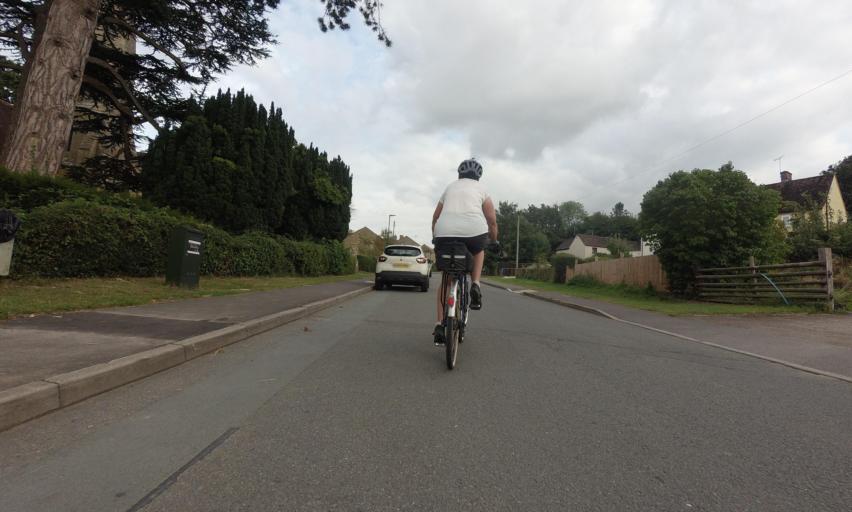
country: GB
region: England
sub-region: Gloucestershire
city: Winchcombe
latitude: 51.9732
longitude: -1.9932
